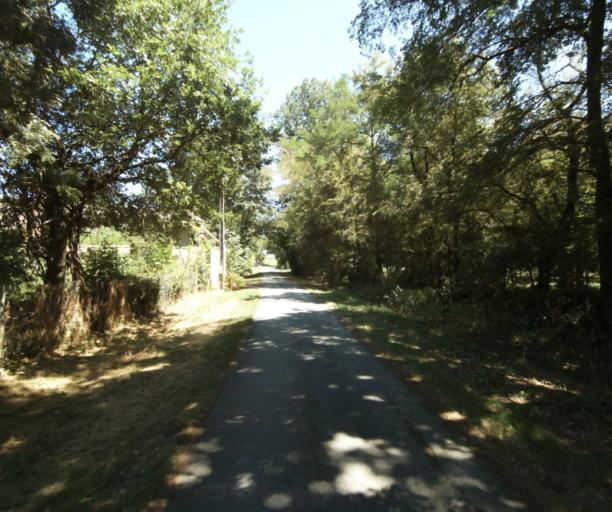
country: FR
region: Midi-Pyrenees
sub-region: Departement de la Haute-Garonne
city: Saint-Felix-Lauragais
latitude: 43.4599
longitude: 1.9428
